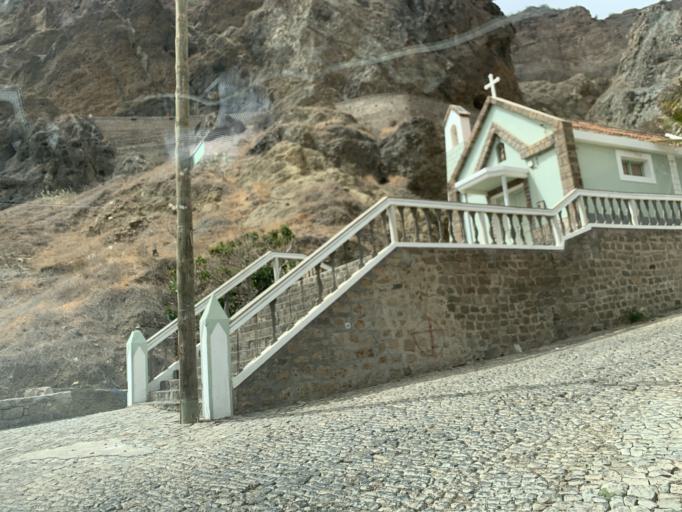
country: CV
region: Brava
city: Vila Nova Sintra
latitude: 14.8738
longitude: -24.7315
